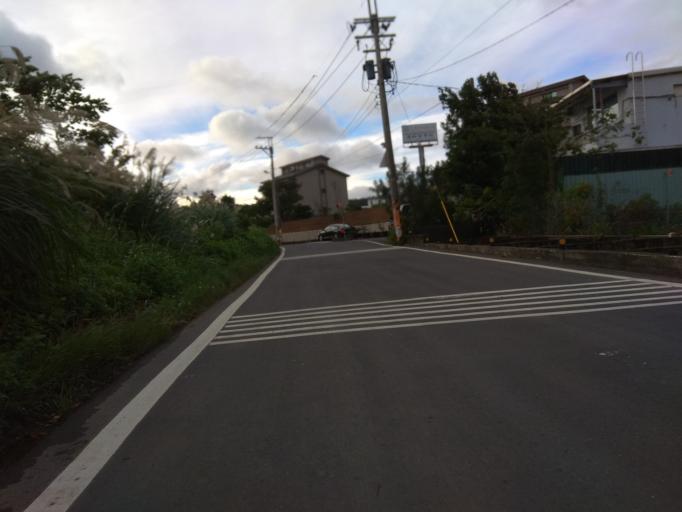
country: TW
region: Taiwan
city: Daxi
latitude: 24.9254
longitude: 121.1965
